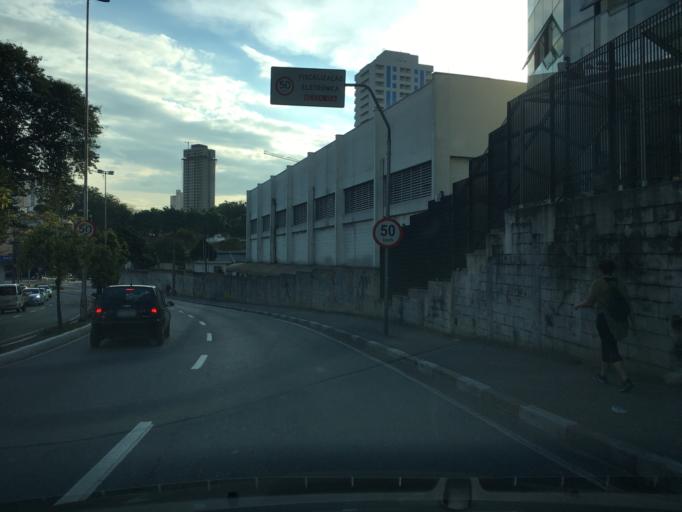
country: BR
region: Sao Paulo
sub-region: Guarulhos
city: Guarulhos
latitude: -23.4654
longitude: -46.5340
